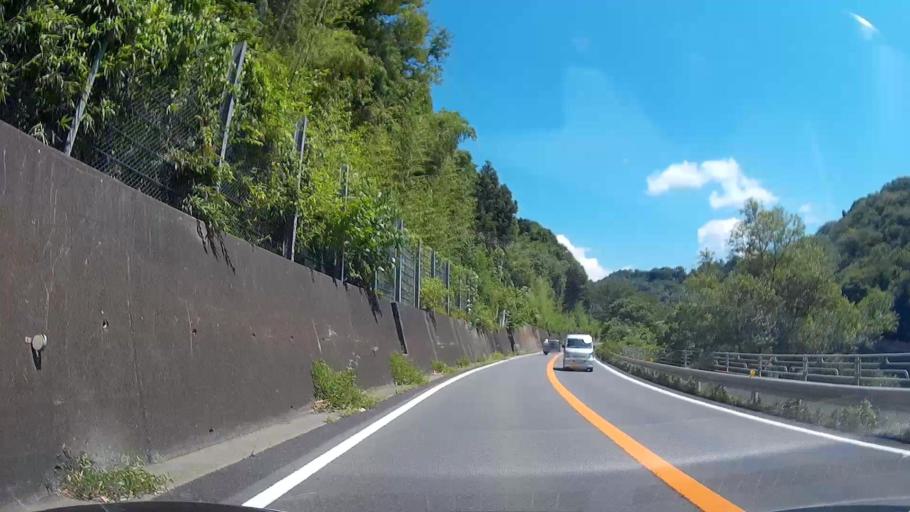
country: JP
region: Gunma
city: Numata
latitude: 36.6258
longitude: 139.0353
